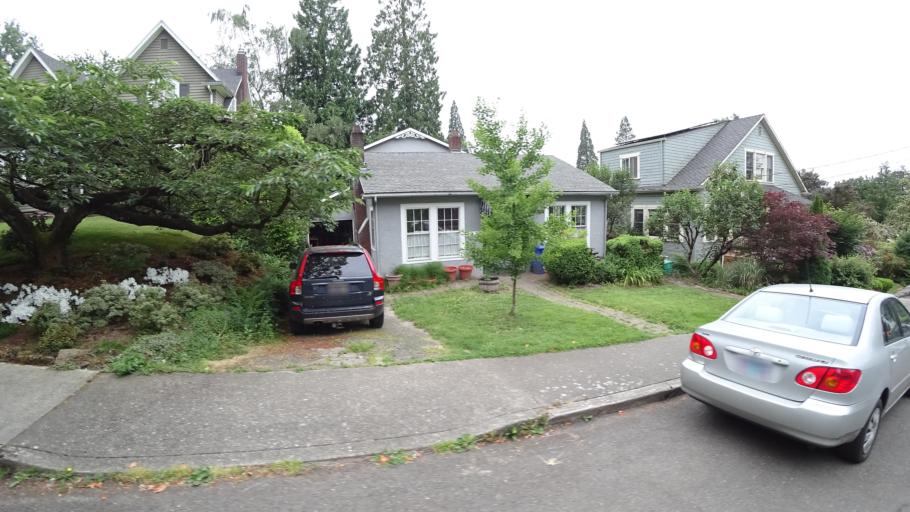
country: US
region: Oregon
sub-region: Multnomah County
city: Portland
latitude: 45.5027
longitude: -122.7062
